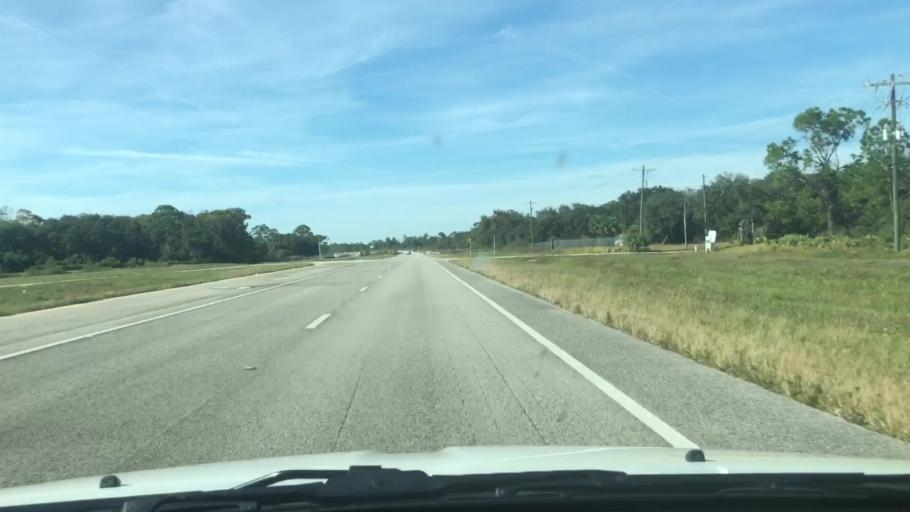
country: US
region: Florida
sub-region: Indian River County
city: Fellsmere
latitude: 27.6864
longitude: -80.8776
